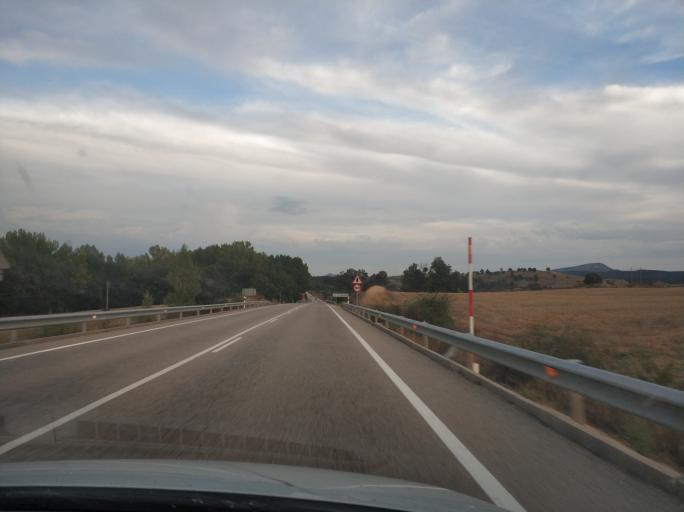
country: ES
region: Castille and Leon
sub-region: Provincia de Burgos
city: Pinilla de los Barruecos
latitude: 41.8978
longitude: -3.2674
